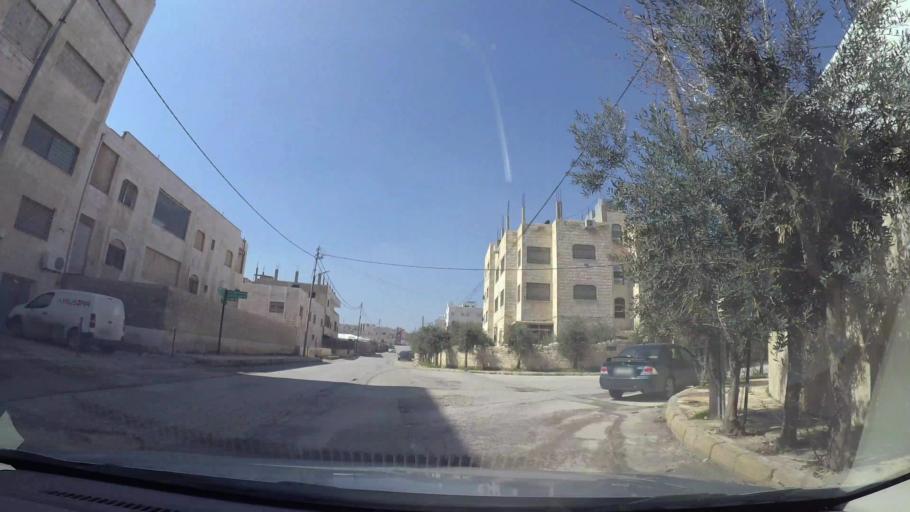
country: JO
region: Amman
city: Al Bunayyat ash Shamaliyah
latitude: 31.8994
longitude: 35.8981
